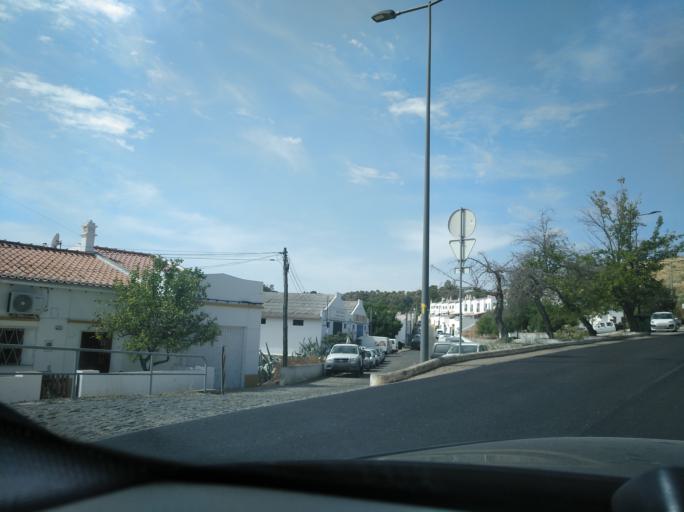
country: PT
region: Beja
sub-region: Mertola
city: Mertola
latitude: 37.6434
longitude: -7.6588
